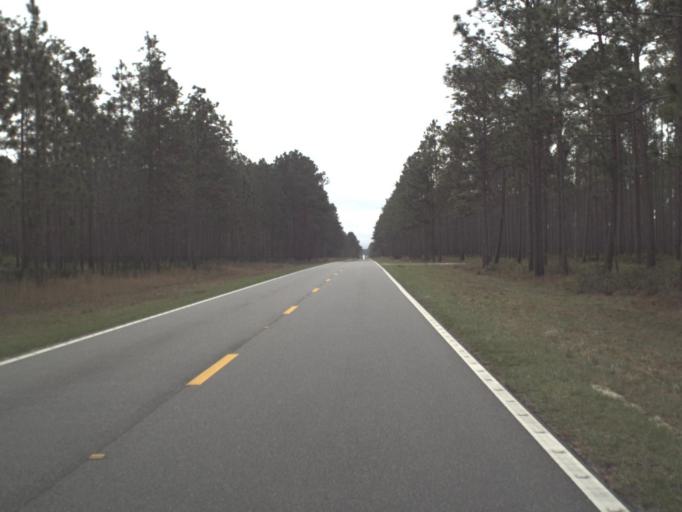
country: US
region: Florida
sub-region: Gulf County
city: Wewahitchka
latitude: 30.1175
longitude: -84.9880
